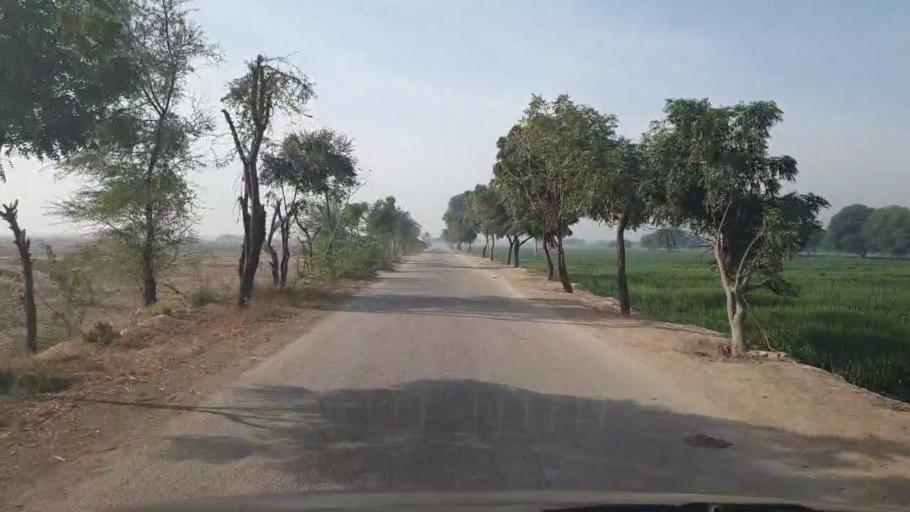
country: PK
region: Sindh
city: Umarkot
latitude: 25.3539
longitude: 69.6993
